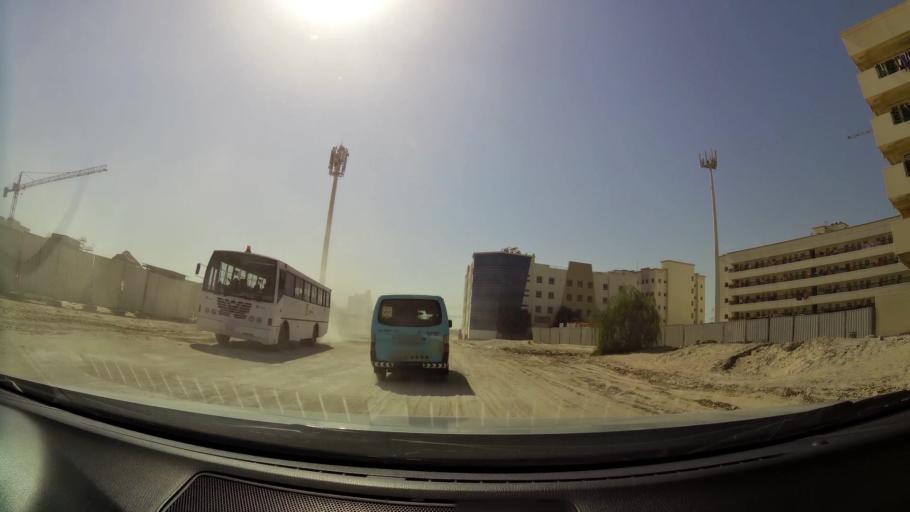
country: AE
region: Dubai
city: Dubai
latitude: 24.9967
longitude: 55.1424
